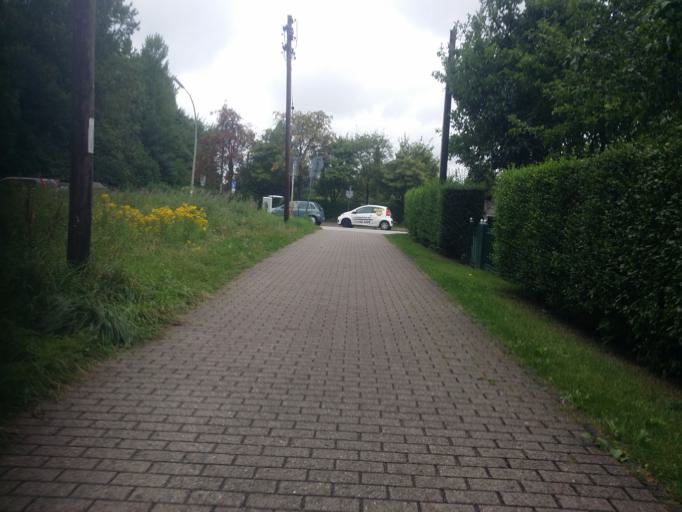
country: DE
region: Hamburg
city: Marienthal
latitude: 53.5487
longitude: 10.0766
